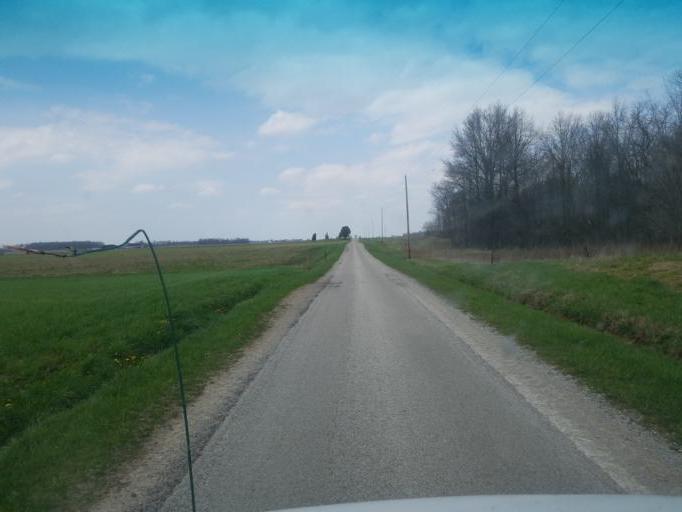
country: US
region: Ohio
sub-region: Crawford County
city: Bucyrus
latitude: 40.9825
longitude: -82.9588
